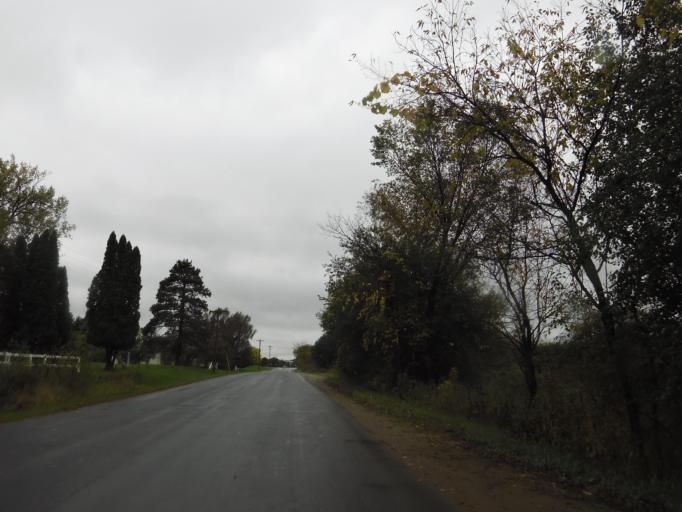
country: US
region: Minnesota
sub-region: Scott County
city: Savage
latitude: 44.7718
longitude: -93.3747
